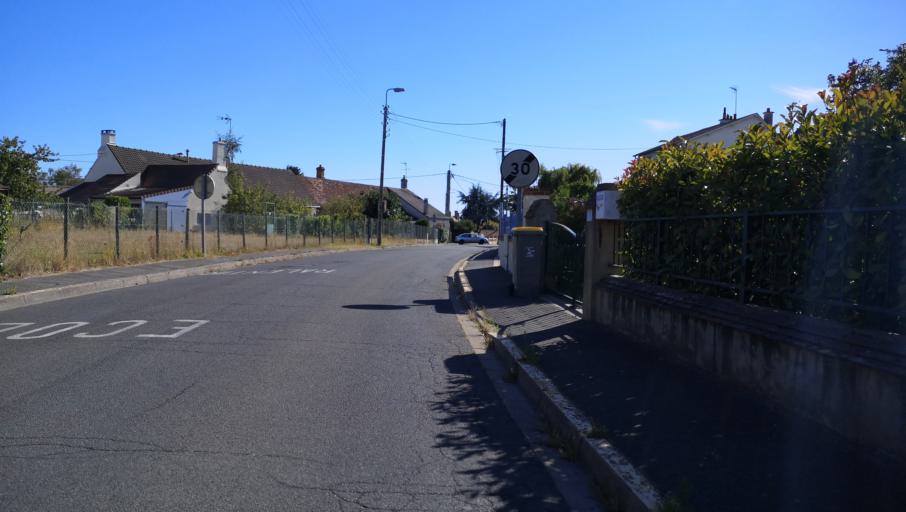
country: FR
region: Centre
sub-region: Departement du Loiret
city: Fleury-les-Aubrais
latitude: 47.9485
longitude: 1.9010
